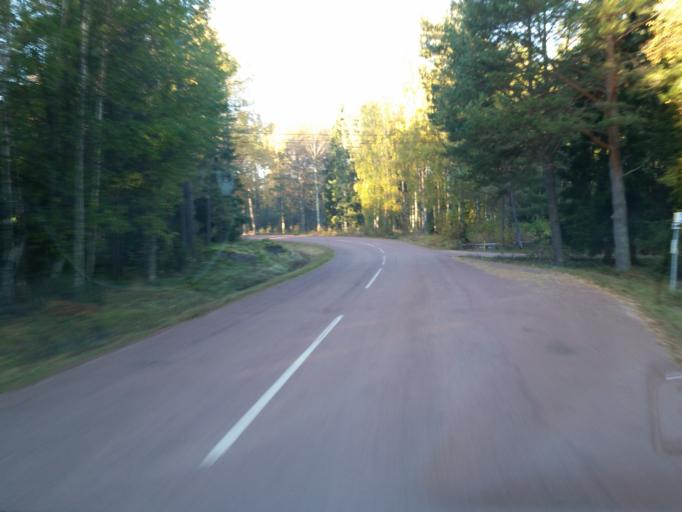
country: AX
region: Alands skaergard
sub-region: Vardoe
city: Vardoe
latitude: 60.2709
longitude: 20.3875
